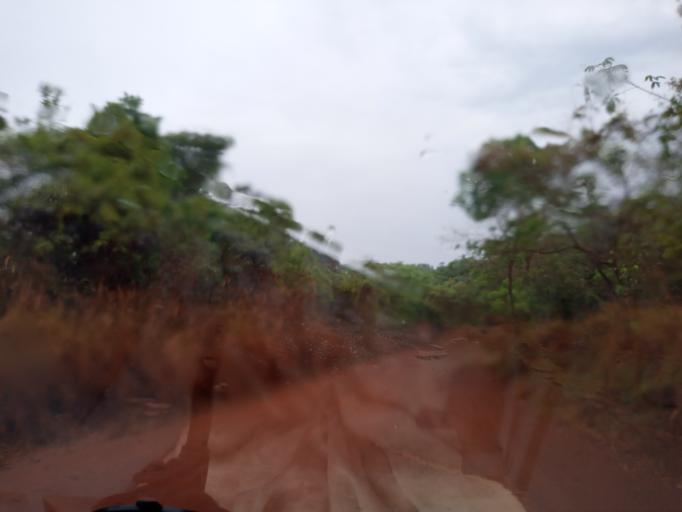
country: BR
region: Minas Gerais
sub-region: Ituiutaba
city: Ituiutaba
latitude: -19.1902
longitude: -49.5104
